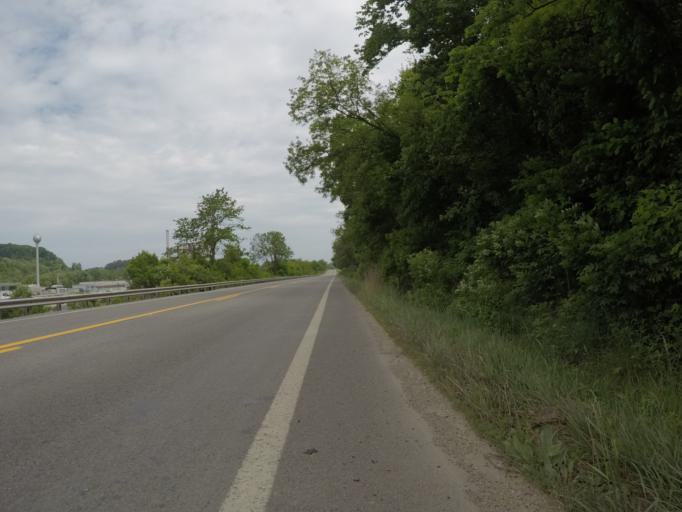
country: US
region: West Virginia
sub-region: Wayne County
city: Kenova
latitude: 38.3540
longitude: -82.5932
